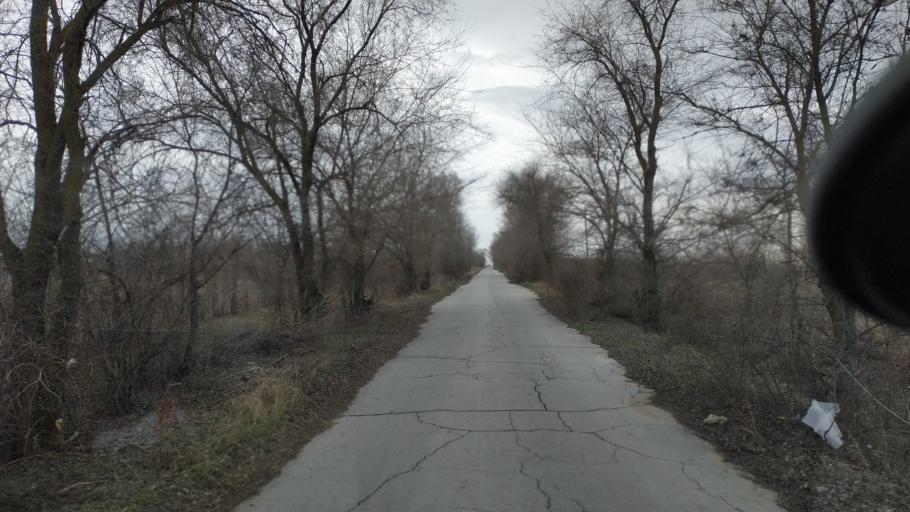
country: MD
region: Telenesti
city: Cocieri
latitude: 47.3280
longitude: 29.0926
